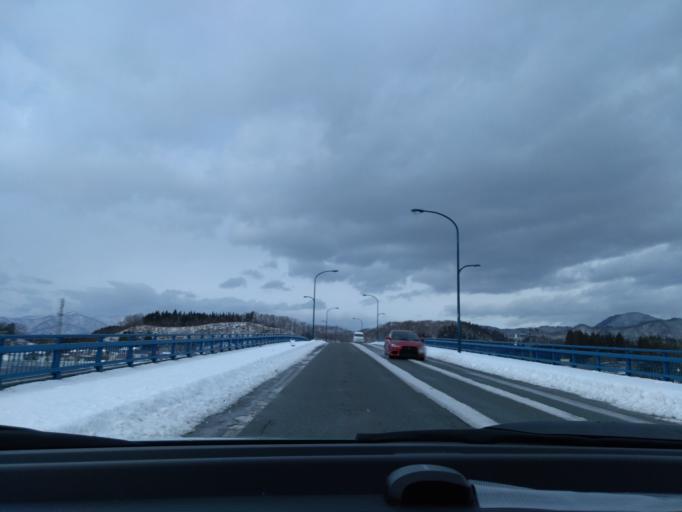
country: JP
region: Akita
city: Kakunodatemachi
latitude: 39.6227
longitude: 140.6303
